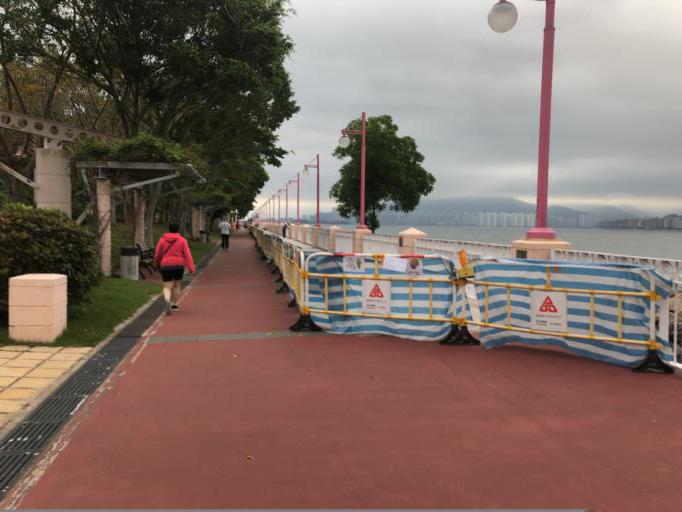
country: HK
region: Tai Po
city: Tai Po
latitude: 22.4518
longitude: 114.1900
